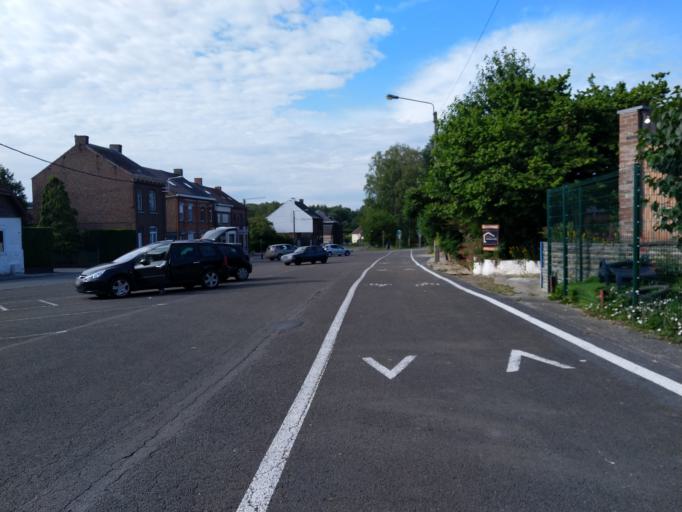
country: BE
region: Wallonia
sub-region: Province du Hainaut
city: Erquelinnes
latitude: 50.3092
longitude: 4.1201
